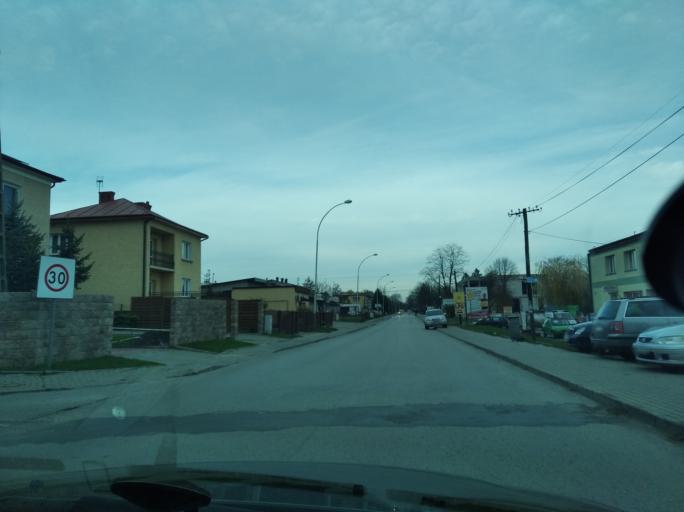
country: PL
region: Subcarpathian Voivodeship
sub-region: Powiat przeworski
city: Przeworsk
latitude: 50.0577
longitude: 22.4771
